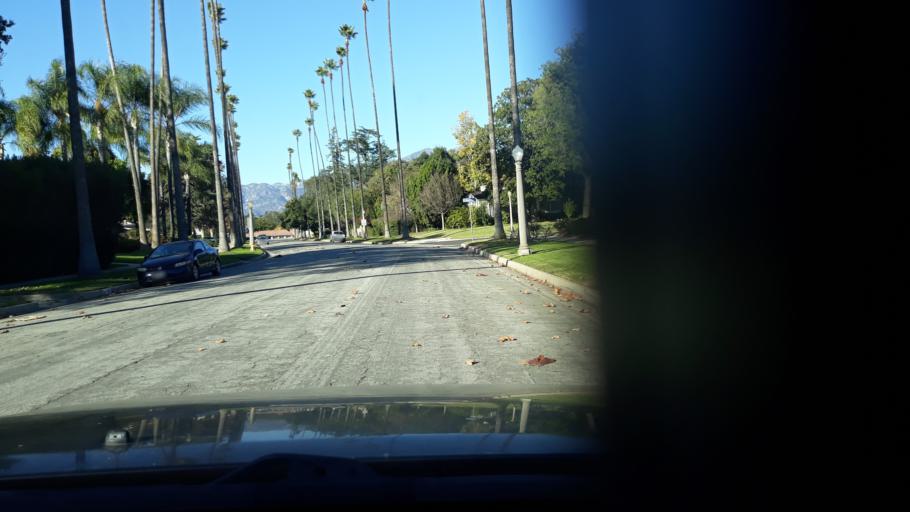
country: US
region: California
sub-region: Los Angeles County
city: San Marino
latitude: 34.1180
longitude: -118.1079
